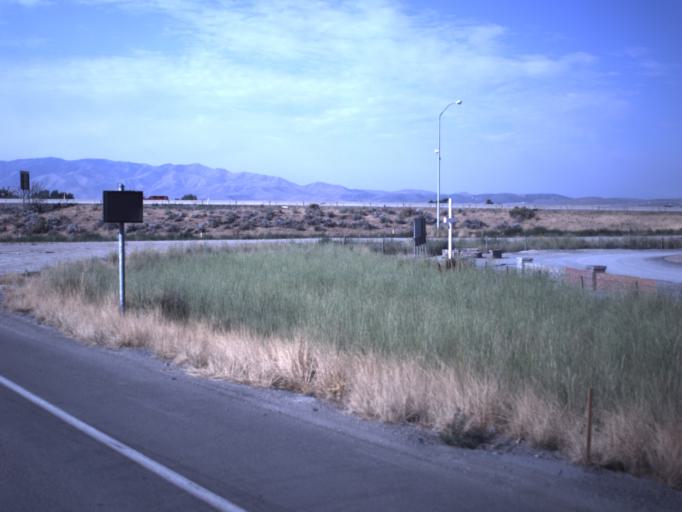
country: US
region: Utah
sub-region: Utah County
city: Lehi
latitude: 40.4155
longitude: -111.8688
